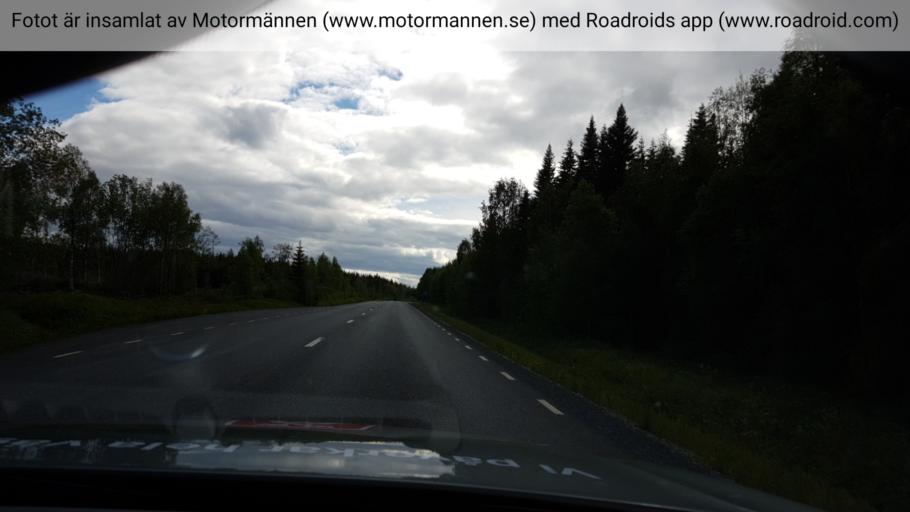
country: SE
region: Jaemtland
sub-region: Stroemsunds Kommun
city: Stroemsund
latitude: 64.1166
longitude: 15.6192
